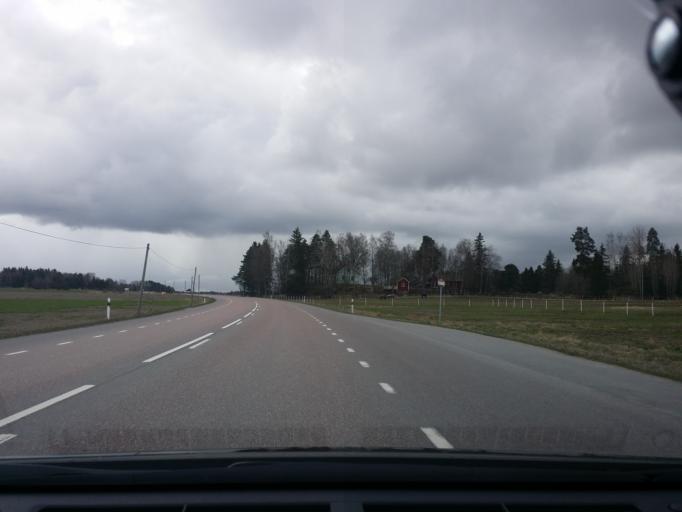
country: SE
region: Uppsala
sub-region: Enkopings Kommun
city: Irsta
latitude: 59.7654
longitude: 16.9156
